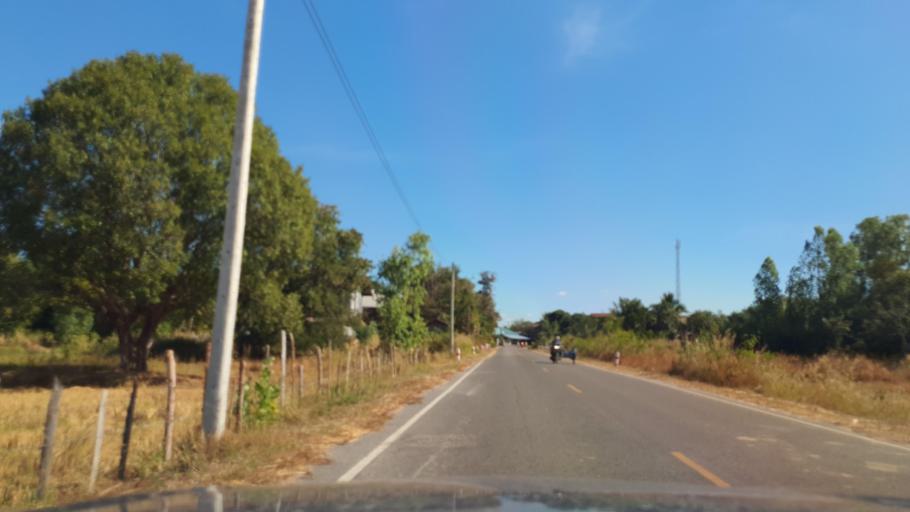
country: TH
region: Kalasin
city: Khao Wong
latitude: 16.7169
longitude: 104.1130
